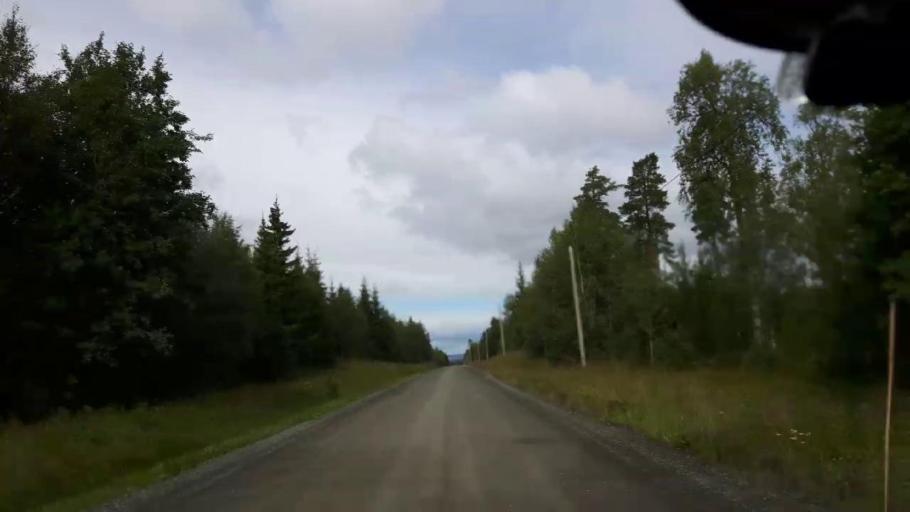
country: SE
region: Jaemtland
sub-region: Krokoms Kommun
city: Krokom
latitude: 63.3820
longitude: 14.1219
